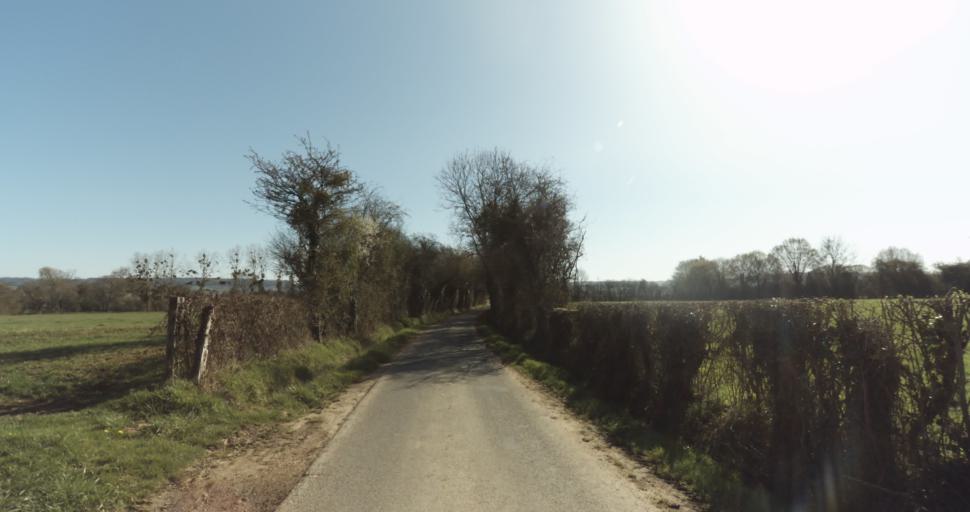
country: FR
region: Lower Normandy
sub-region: Departement du Calvados
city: Saint-Pierre-sur-Dives
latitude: 48.9681
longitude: 0.0050
